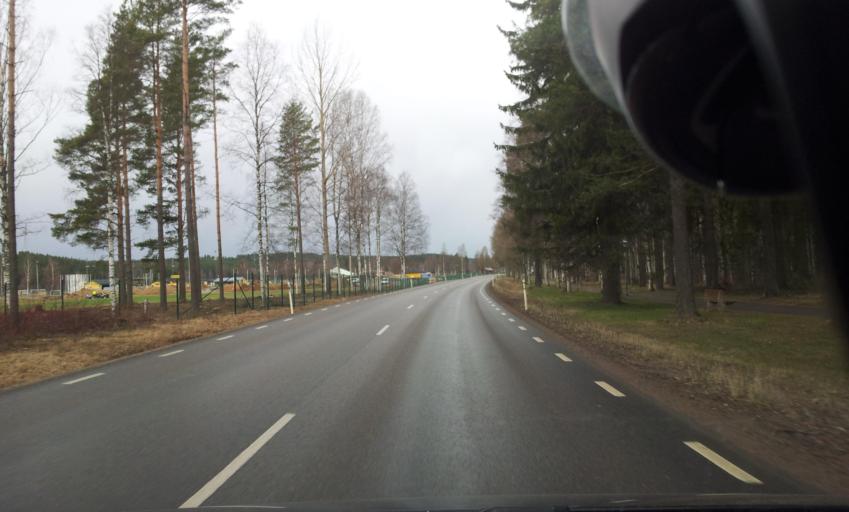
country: SE
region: Gaevleborg
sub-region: Ljusdals Kommun
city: Ljusdal
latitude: 61.8195
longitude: 16.0935
